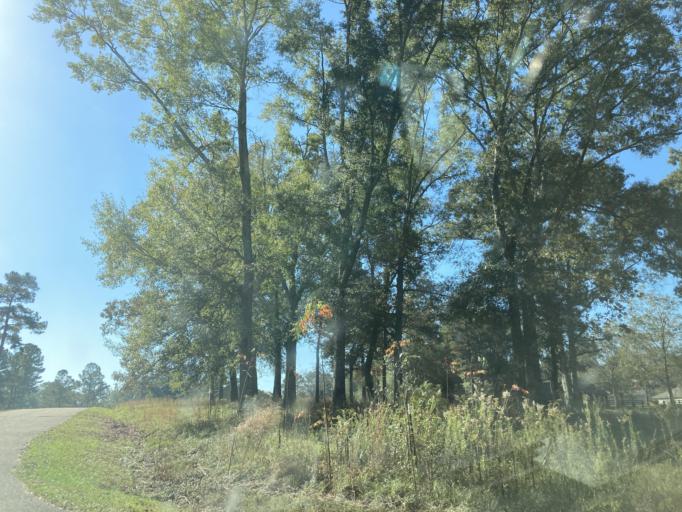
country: US
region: Mississippi
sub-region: Lamar County
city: Sumrall
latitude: 31.3502
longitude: -89.4959
